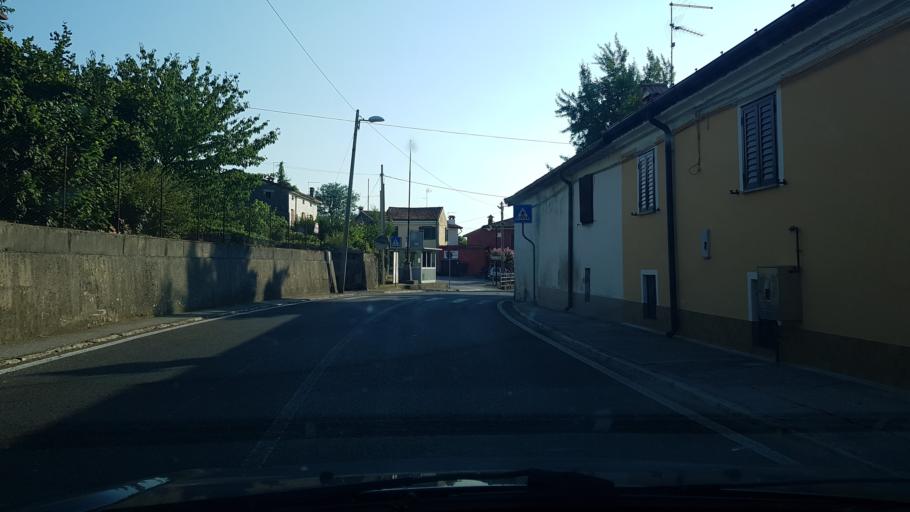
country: IT
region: Friuli Venezia Giulia
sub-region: Provincia di Gorizia
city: Gradisca d'Isonzo
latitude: 45.8872
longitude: 13.5158
